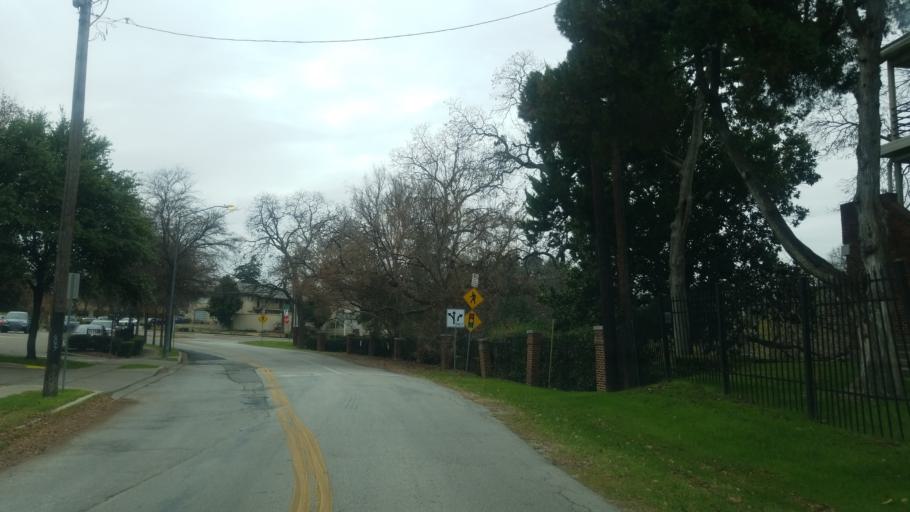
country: US
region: Texas
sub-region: Dallas County
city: Highland Park
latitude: 32.8194
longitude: -96.8200
